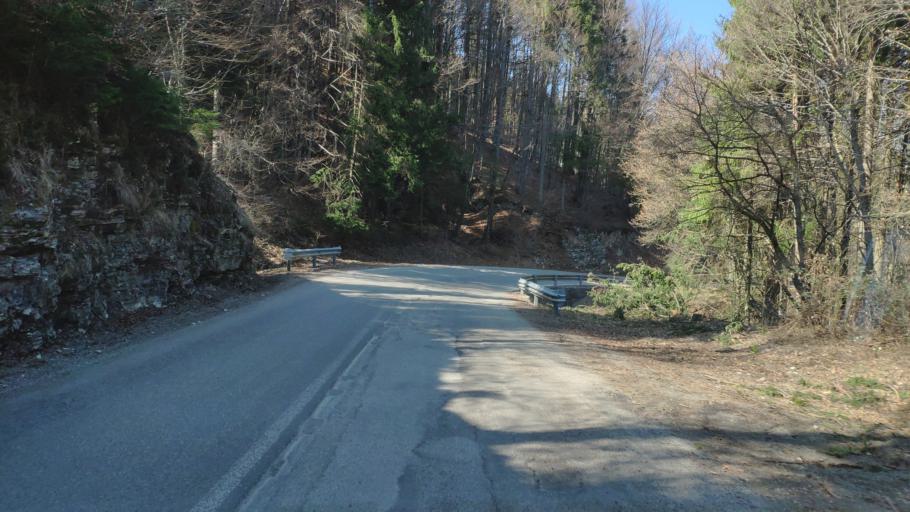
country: IT
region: Veneto
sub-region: Provincia di Vicenza
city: Enego
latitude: 45.9321
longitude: 11.7025
